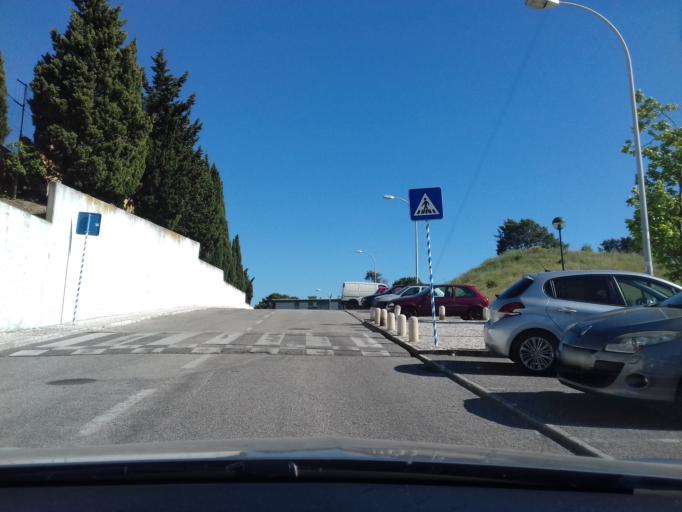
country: PT
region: Lisbon
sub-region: Oeiras
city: Oeiras
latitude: 38.6987
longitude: -9.3085
